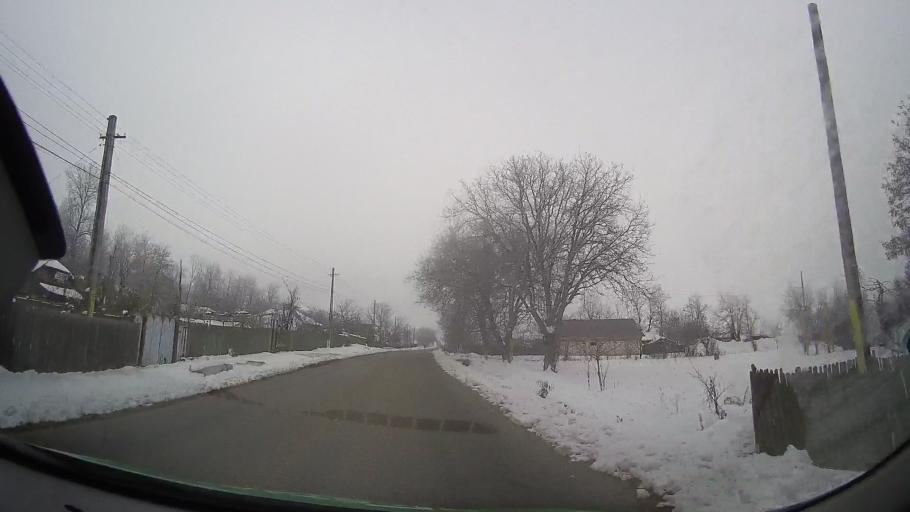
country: RO
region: Bacau
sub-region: Comuna Stanisesti
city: Stanisesti
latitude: 46.4169
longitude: 27.2683
